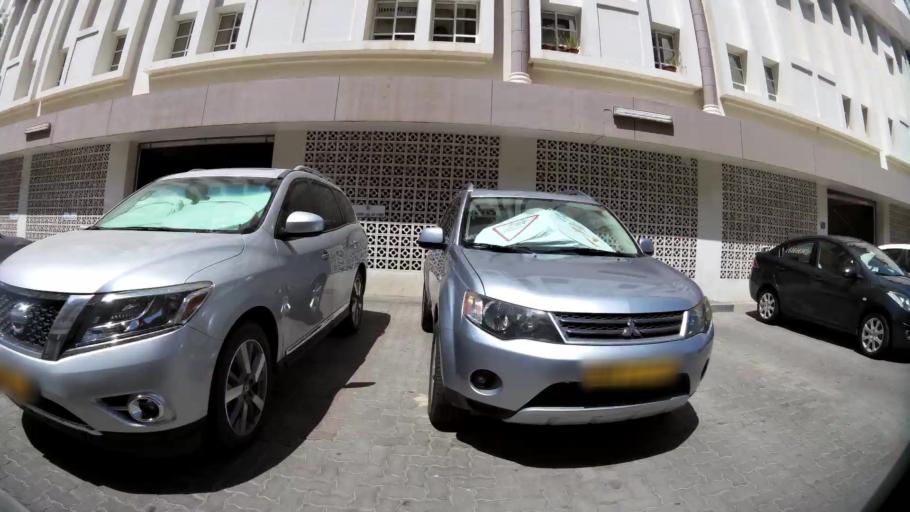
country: OM
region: Muhafazat Masqat
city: Muscat
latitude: 23.5973
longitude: 58.5404
